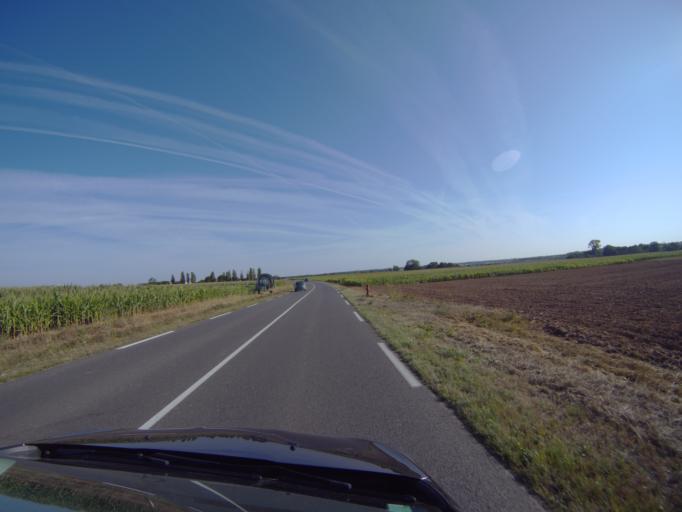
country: FR
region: Pays de la Loire
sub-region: Departement de la Vendee
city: Jard-sur-Mer
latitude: 46.4384
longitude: -1.5785
